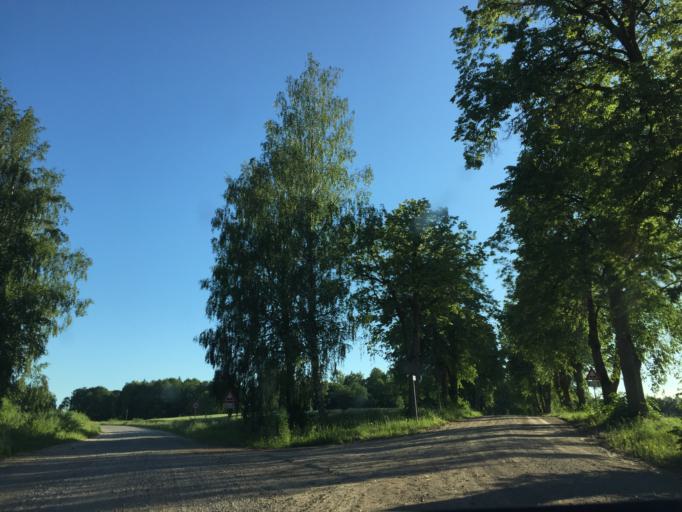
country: LV
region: Broceni
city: Broceni
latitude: 56.8247
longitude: 22.5494
